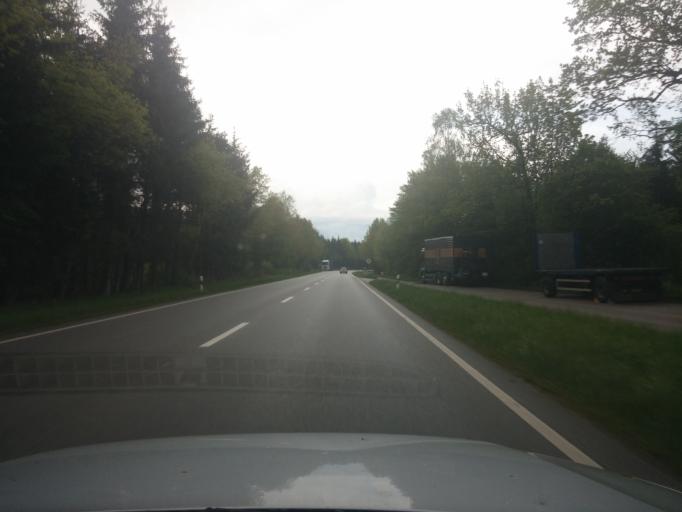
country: DE
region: Bavaria
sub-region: Upper Bavaria
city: Putzbrunn
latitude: 48.0889
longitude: 11.7212
